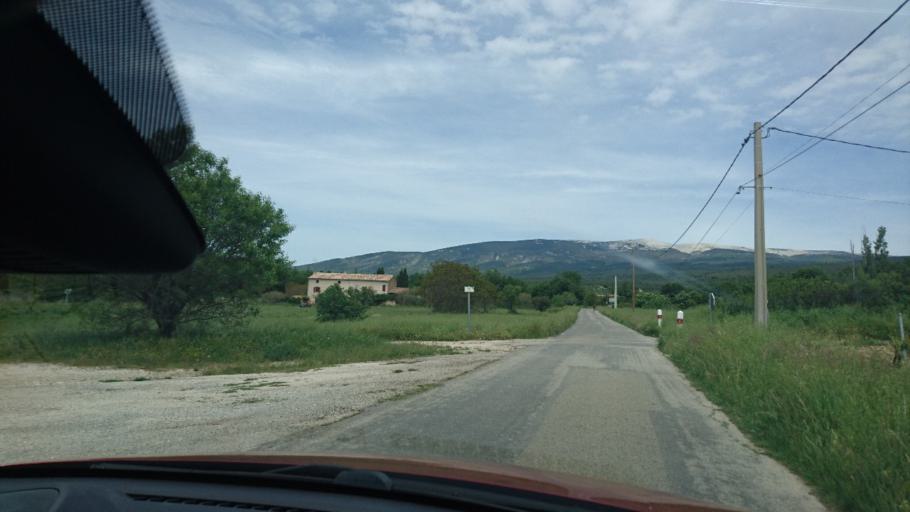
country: FR
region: Provence-Alpes-Cote d'Azur
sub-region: Departement du Vaucluse
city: Villes-sur-Auzon
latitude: 44.0909
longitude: 5.2387
